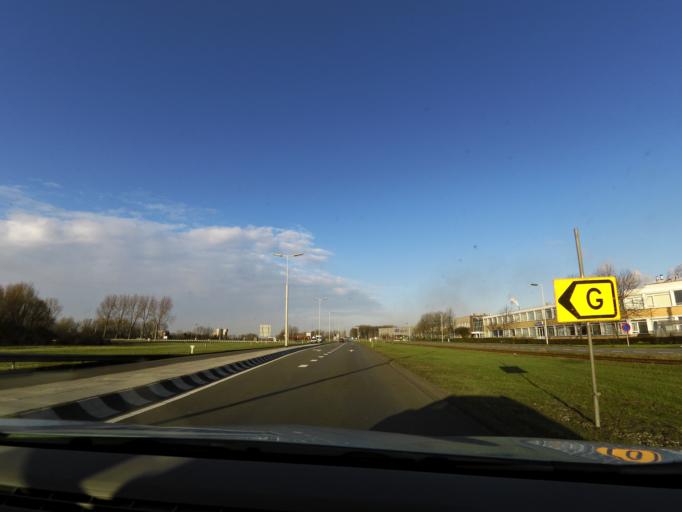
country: NL
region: South Holland
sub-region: Gemeente Maassluis
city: Maassluis
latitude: 51.8939
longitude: 4.2634
